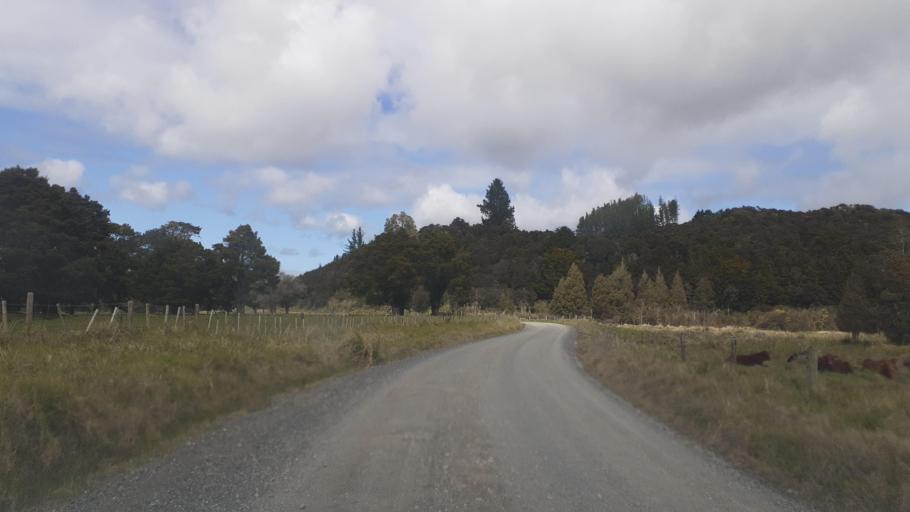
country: NZ
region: Northland
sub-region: Far North District
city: Moerewa
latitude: -35.5111
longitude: 173.9799
